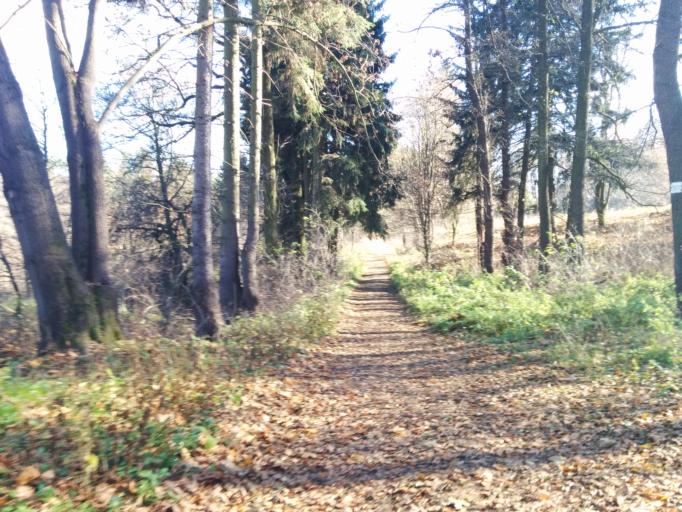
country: CZ
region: Vysocina
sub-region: Okres Jihlava
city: Jihlava
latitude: 49.4138
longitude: 15.5528
